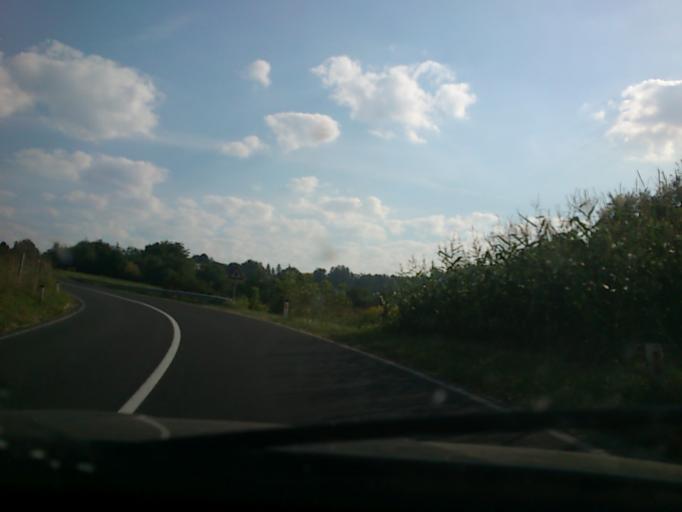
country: SI
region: Starse
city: Starse
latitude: 46.4916
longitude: 15.7828
